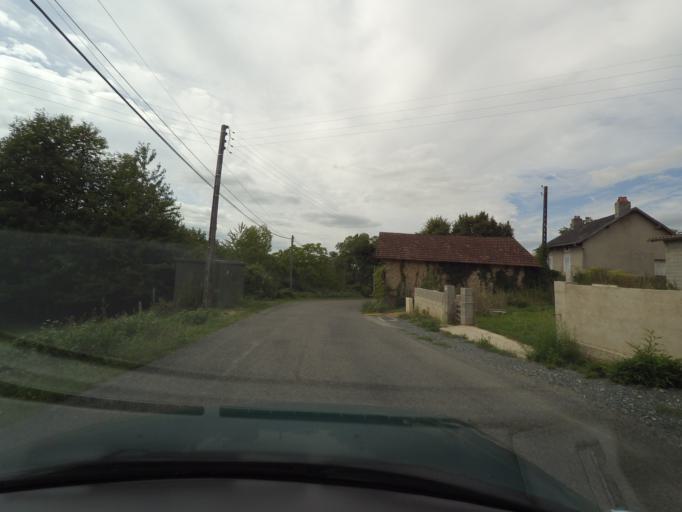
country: FR
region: Limousin
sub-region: Departement de la Haute-Vienne
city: Bussiere-Galant
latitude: 45.6716
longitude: 1.0785
